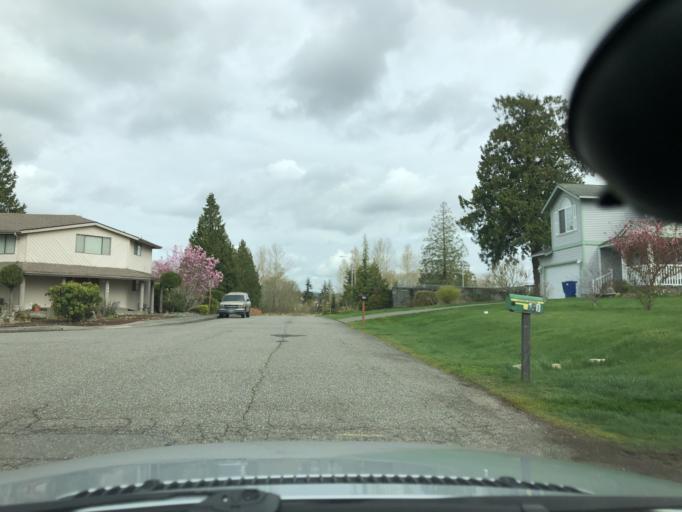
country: US
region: Washington
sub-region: Whatcom County
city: Blaine
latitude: 48.9997
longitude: -122.7401
